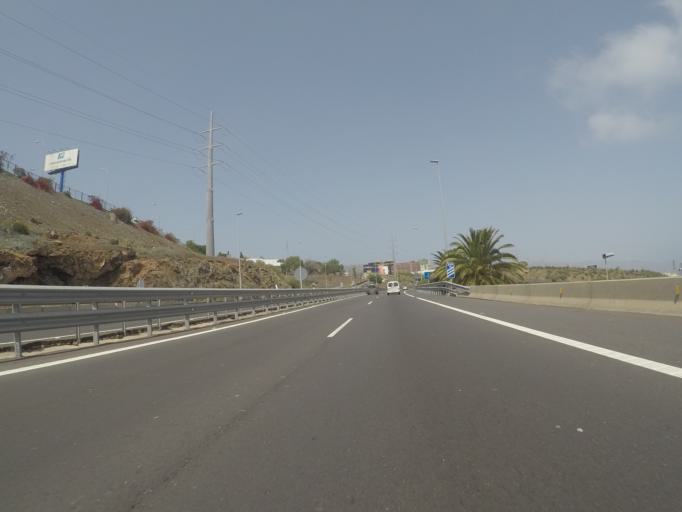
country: ES
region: Canary Islands
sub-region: Provincia de Santa Cruz de Tenerife
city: Santa Cruz de Tenerife
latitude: 28.4420
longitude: -16.2783
